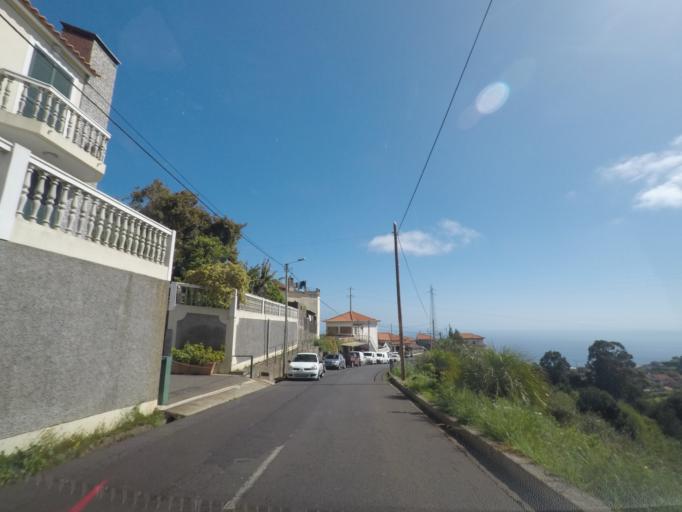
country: PT
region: Madeira
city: Ponta do Sol
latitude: 32.7024
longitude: -17.1097
